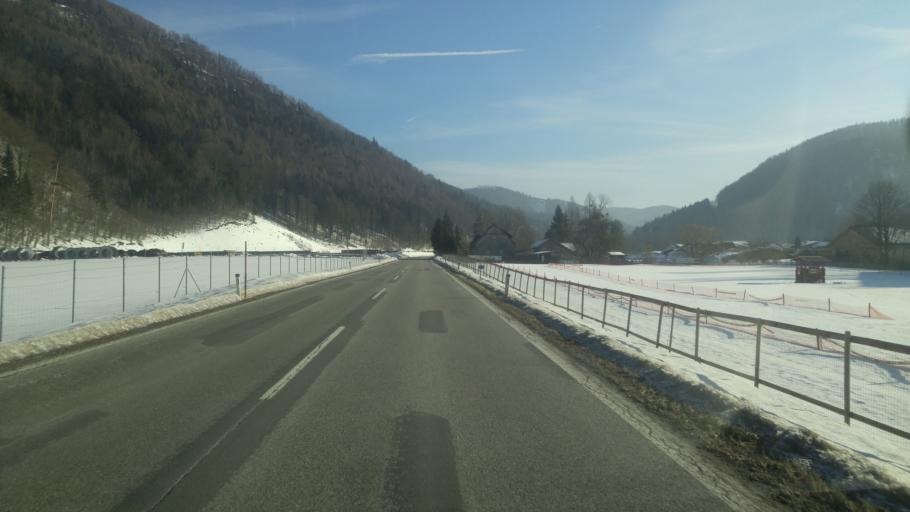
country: AT
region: Lower Austria
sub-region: Politischer Bezirk Lilienfeld
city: Hohenberg
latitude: 47.9316
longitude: 15.6065
